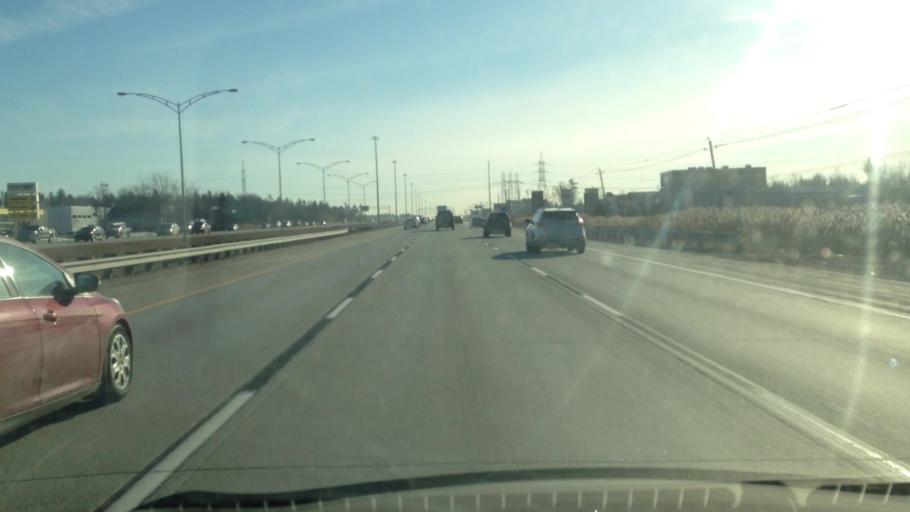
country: CA
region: Quebec
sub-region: Laurentides
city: Blainville
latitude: 45.6867
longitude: -73.9286
